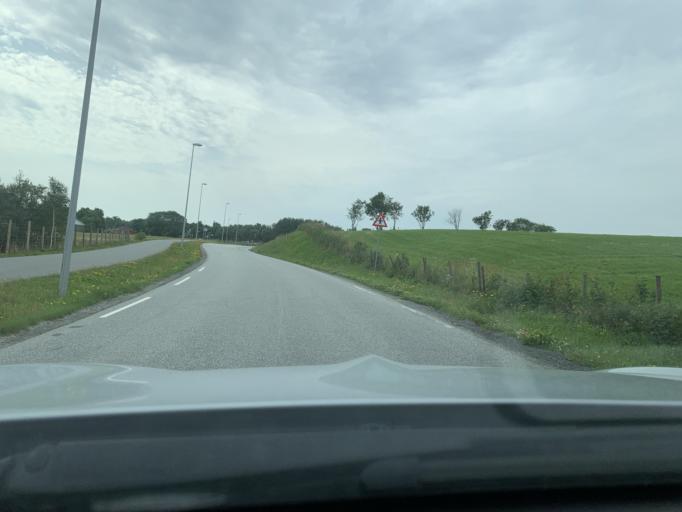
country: NO
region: Rogaland
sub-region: Time
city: Bryne
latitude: 58.7627
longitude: 5.7113
